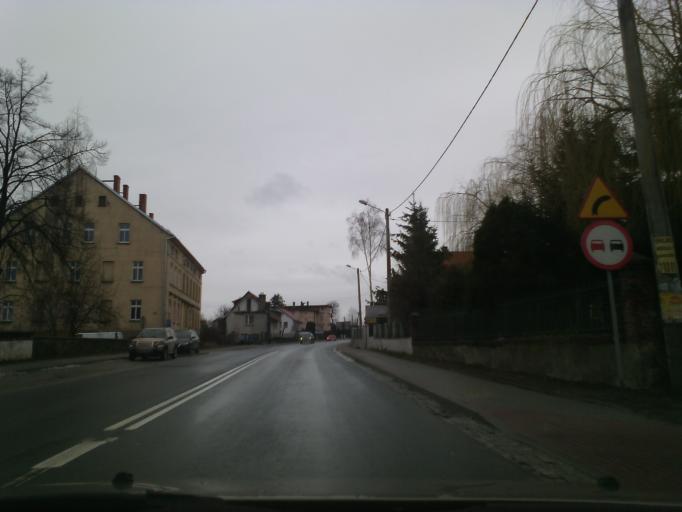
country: PL
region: Lower Silesian Voivodeship
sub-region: Powiat swidnicki
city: Swidnica
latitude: 50.8401
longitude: 16.4480
